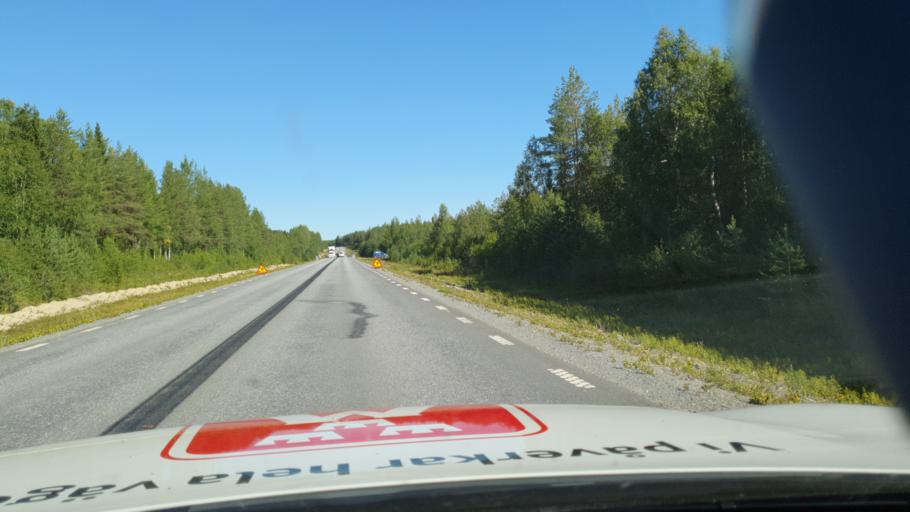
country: SE
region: Vaesterbotten
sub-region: Dorotea Kommun
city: Dorotea
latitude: 64.2648
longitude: 16.4934
